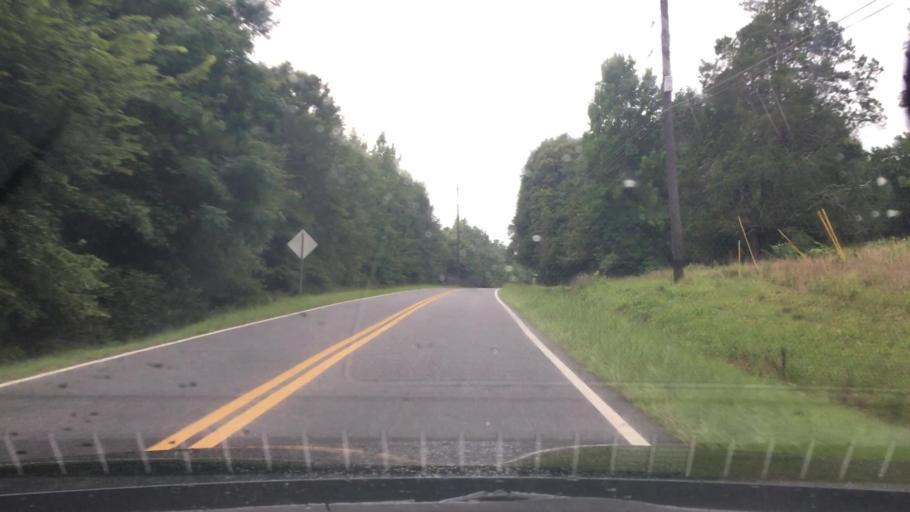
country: US
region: Georgia
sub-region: Spalding County
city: Experiment
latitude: 33.2547
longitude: -84.3883
